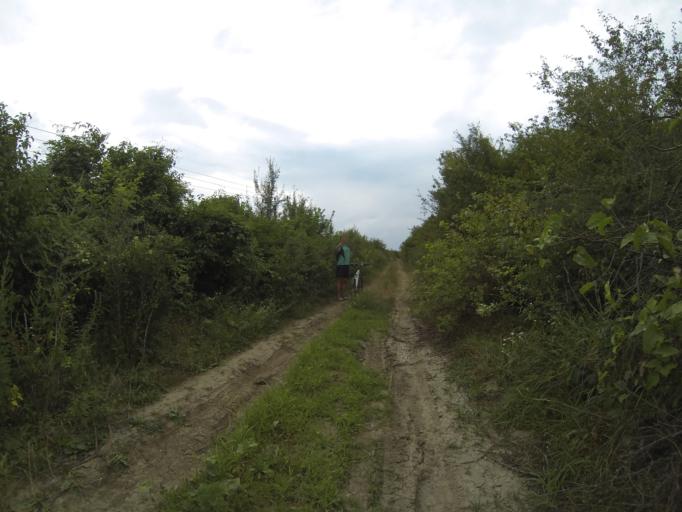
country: RO
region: Dolj
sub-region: Comuna Cotofenii din Fata
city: Cotofenii din Fata
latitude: 44.4820
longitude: 23.6851
